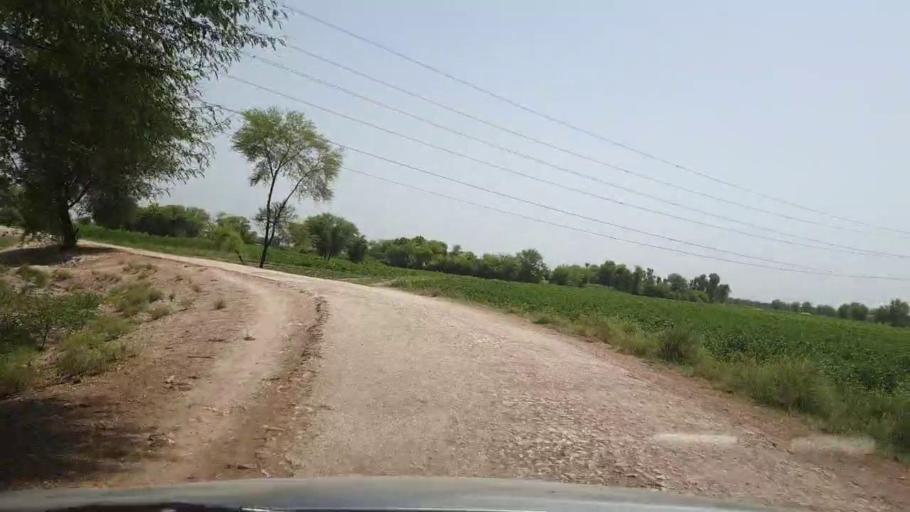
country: PK
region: Sindh
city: Pano Aqil
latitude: 27.8265
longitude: 69.2137
